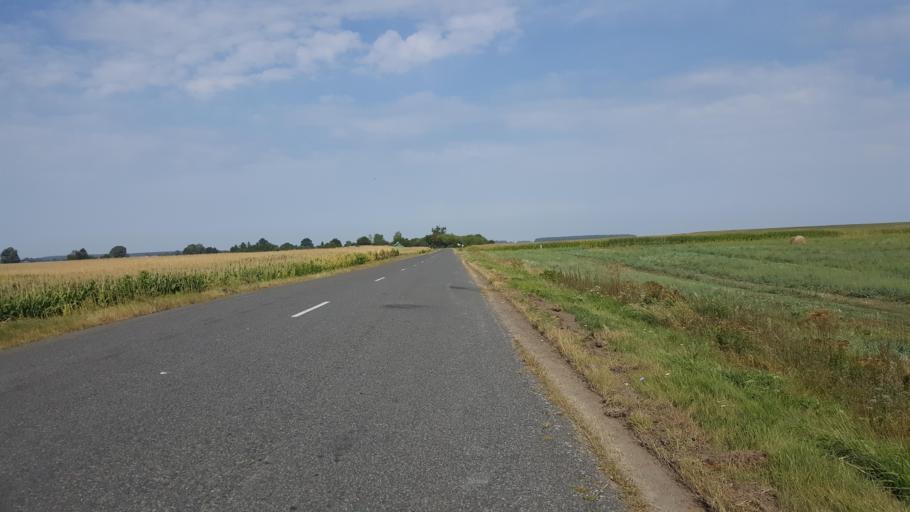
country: BY
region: Brest
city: Kamyanyets
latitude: 52.4216
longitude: 23.7750
